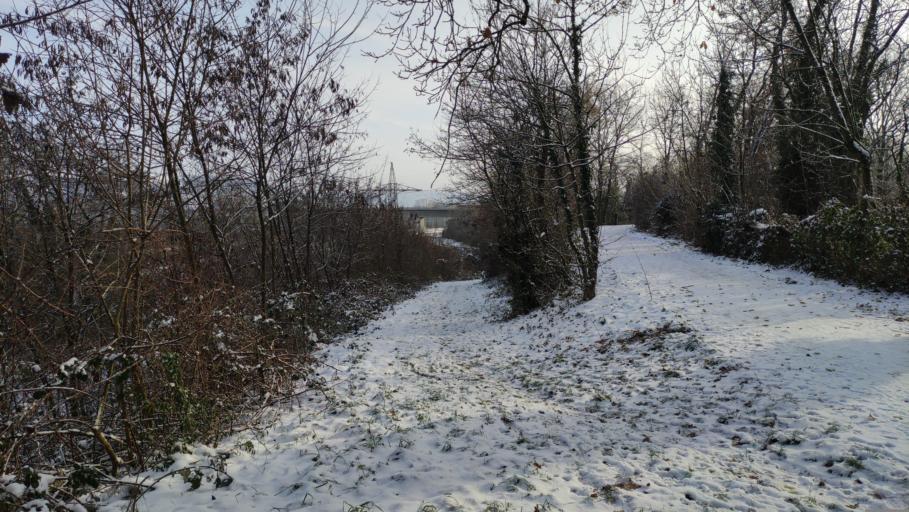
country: DE
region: Baden-Wuerttemberg
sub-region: Freiburg Region
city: Weil am Rhein
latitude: 47.6060
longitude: 7.6082
